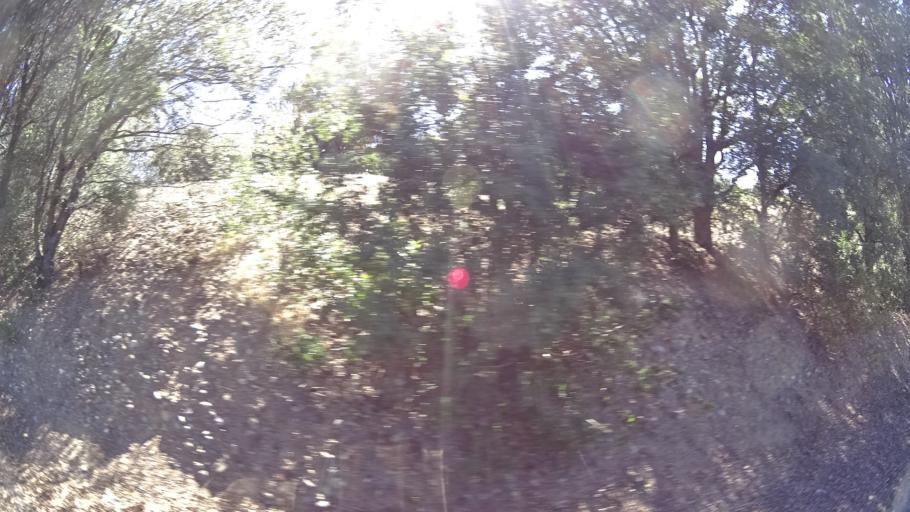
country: US
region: California
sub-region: Calaveras County
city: Valley Springs
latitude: 38.1651
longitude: -120.8496
